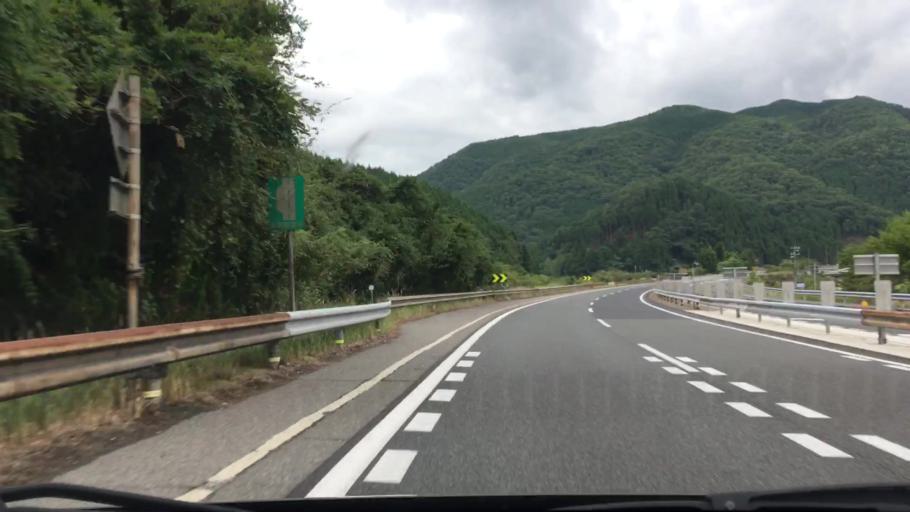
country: JP
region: Okayama
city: Niimi
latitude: 35.0055
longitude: 133.4860
